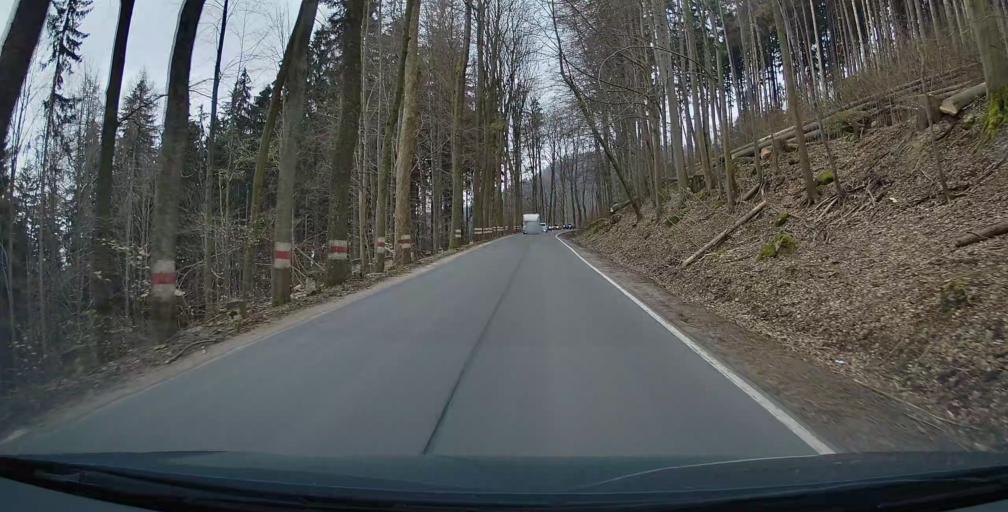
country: PL
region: Lower Silesian Voivodeship
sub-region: Powiat klodzki
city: Radkow
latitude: 50.4908
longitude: 16.3708
